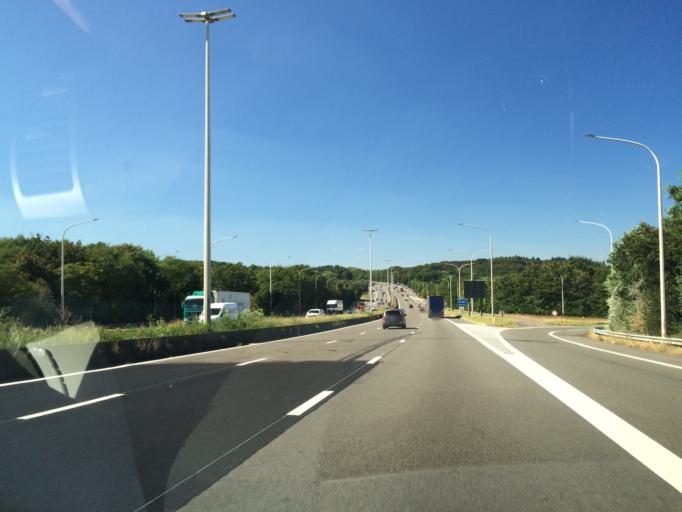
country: BE
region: Wallonia
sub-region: Province du Brabant Wallon
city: Wavre
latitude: 50.7079
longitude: 4.6082
